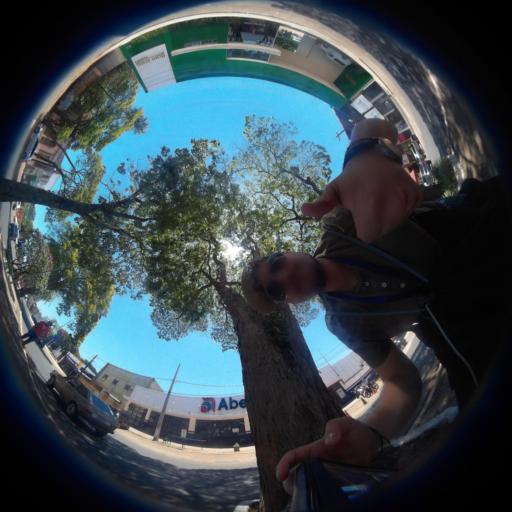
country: BR
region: Mato Grosso do Sul
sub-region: Ponta Pora
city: Ponta Pora
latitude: -22.5348
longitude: -55.7301
